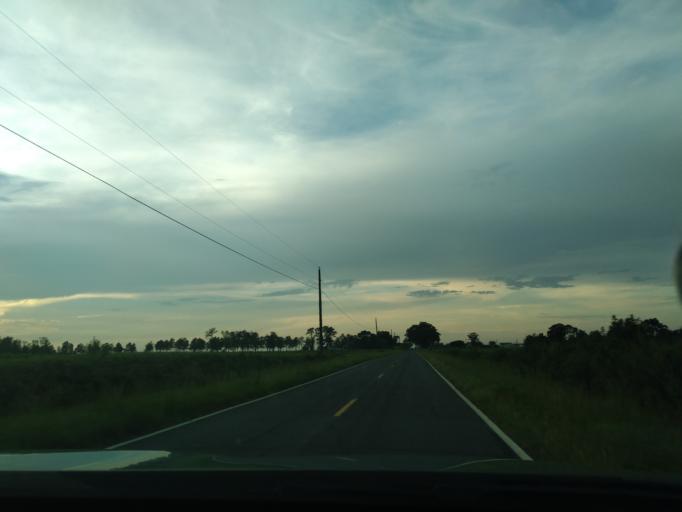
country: US
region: North Carolina
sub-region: Washington County
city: Plymouth
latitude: 35.9307
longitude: -76.6402
